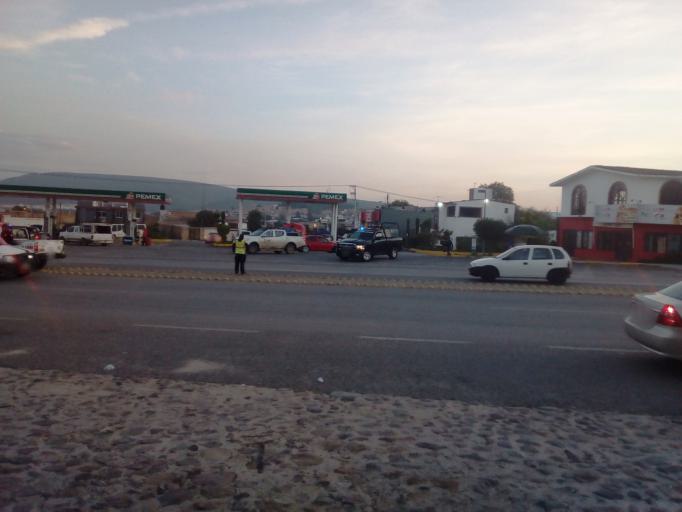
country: MX
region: Guerrero
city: San Luis de la Paz
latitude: 21.2881
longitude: -100.5097
